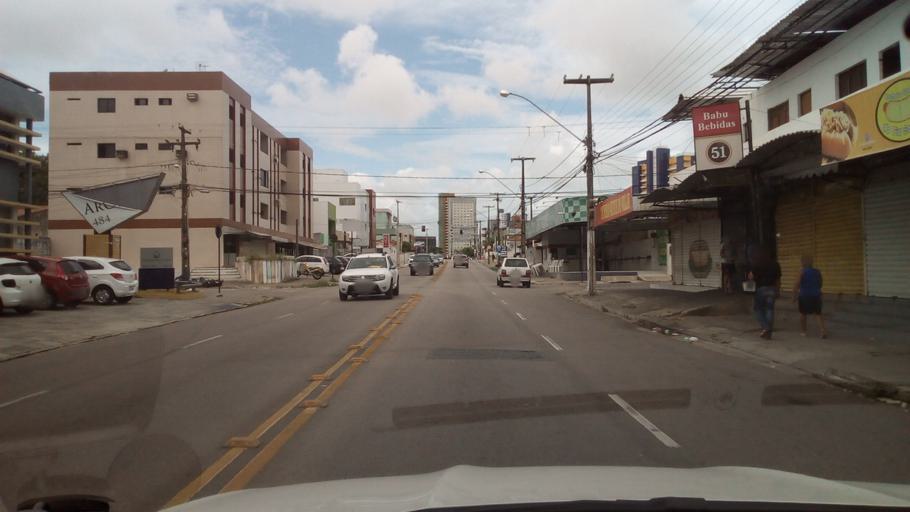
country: BR
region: Paraiba
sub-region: Joao Pessoa
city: Joao Pessoa
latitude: -7.1252
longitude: -34.8599
